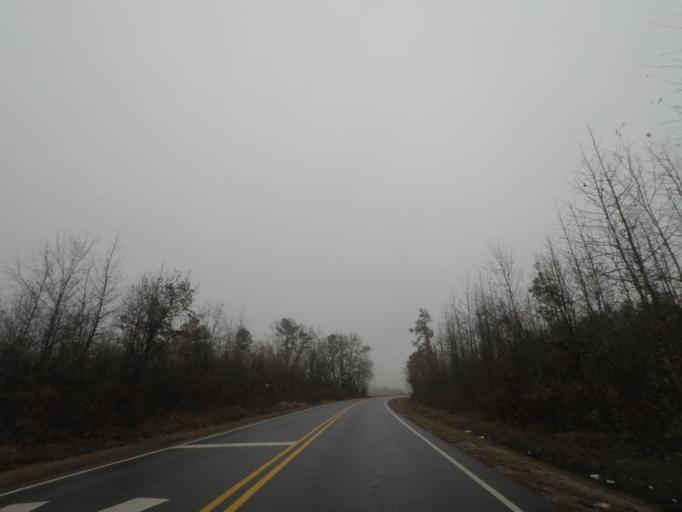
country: US
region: North Carolina
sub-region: Scotland County
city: Laurinburg
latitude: 34.8090
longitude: -79.4437
